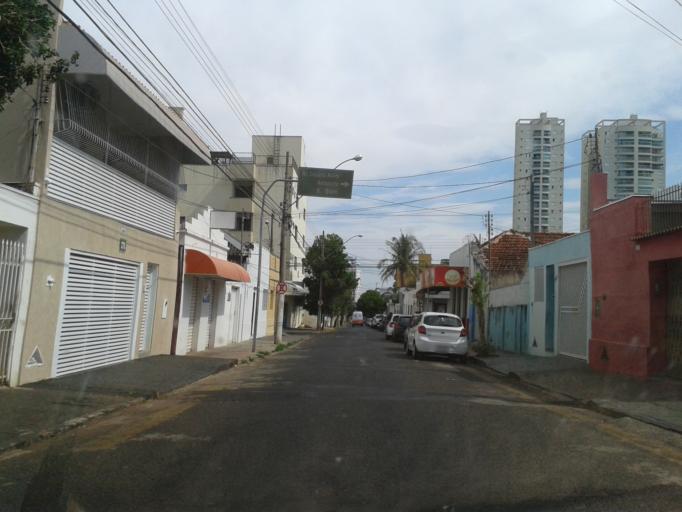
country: BR
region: Minas Gerais
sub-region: Uberlandia
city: Uberlandia
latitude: -18.9180
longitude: -48.2722
